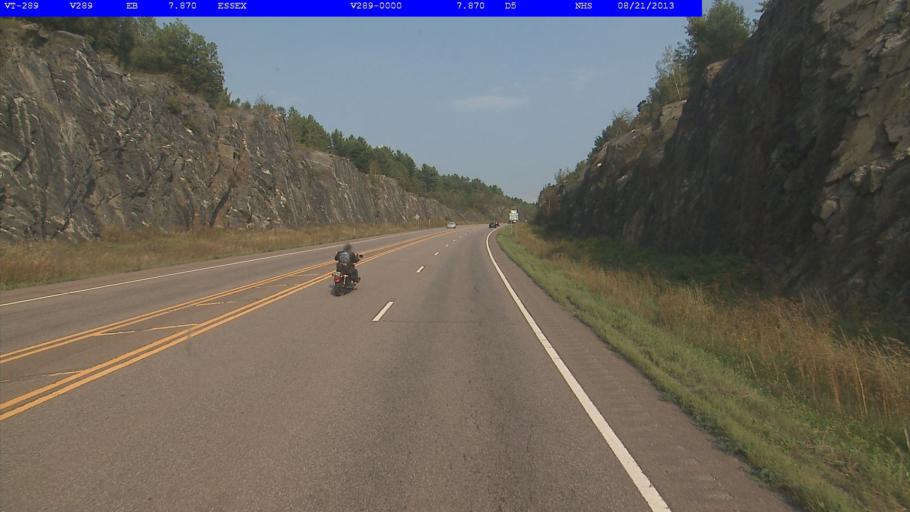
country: US
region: Vermont
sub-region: Chittenden County
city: Essex Junction
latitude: 44.5176
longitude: -73.1160
